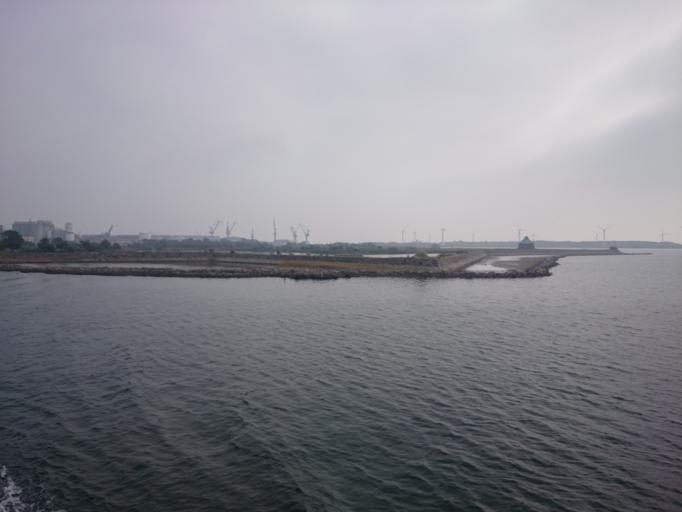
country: SE
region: Skane
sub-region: Landskrona
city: Landskrona
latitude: 55.8671
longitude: 12.8133
